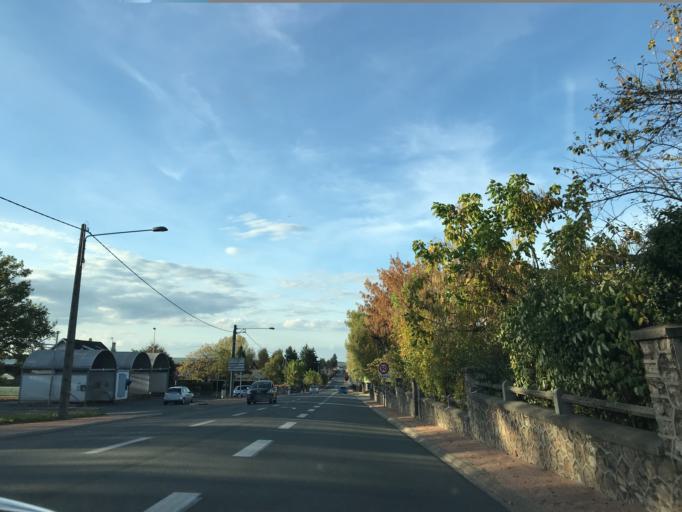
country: FR
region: Auvergne
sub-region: Departement du Puy-de-Dome
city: Puy-Guillaume
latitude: 45.9495
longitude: 3.4812
